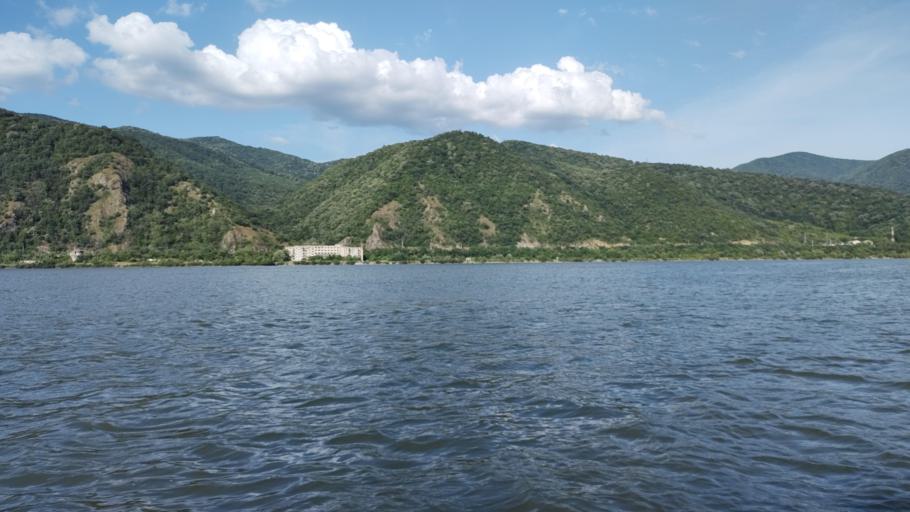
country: RO
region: Caras-Severin
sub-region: Comuna Berzasca
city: Berzasca
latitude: 44.6275
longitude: 21.9946
